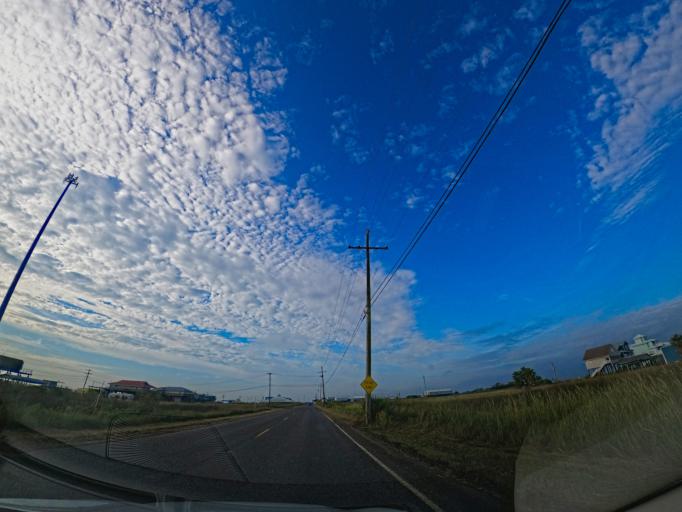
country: US
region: Louisiana
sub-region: Terrebonne Parish
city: Dulac
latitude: 29.2497
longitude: -90.6613
